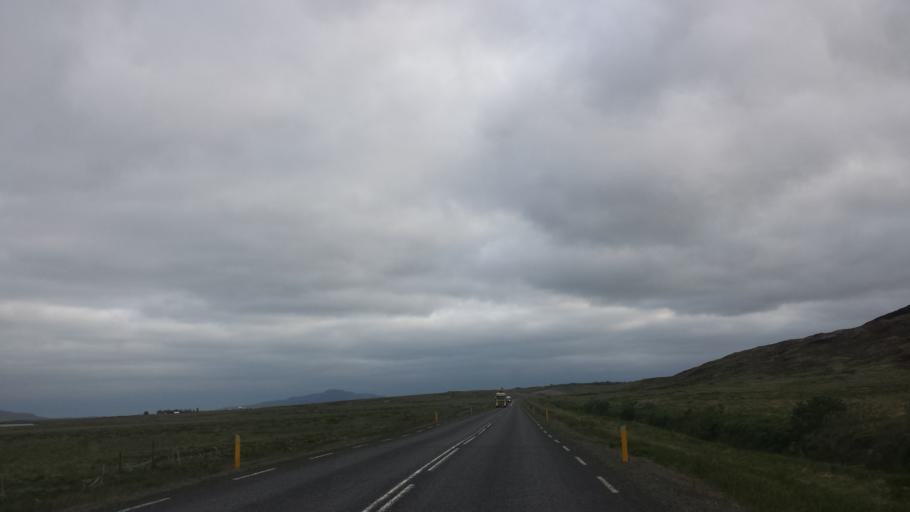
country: IS
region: South
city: Selfoss
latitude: 64.1350
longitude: -20.5771
